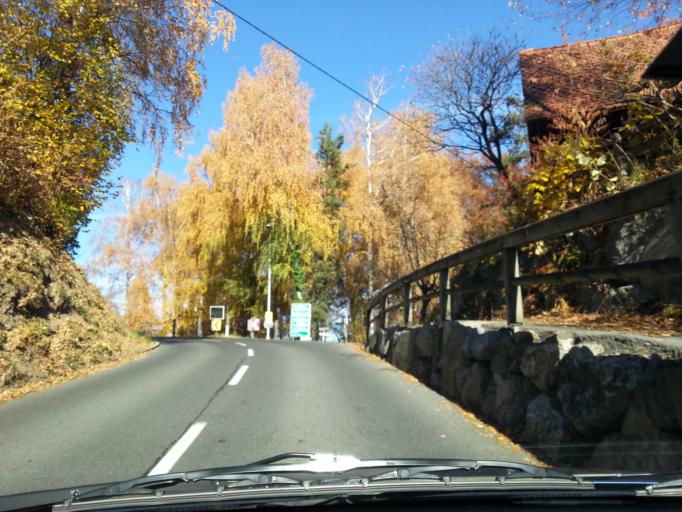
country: AT
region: Styria
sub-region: Politischer Bezirk Deutschlandsberg
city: Gundersdorf
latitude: 46.9385
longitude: 15.2450
